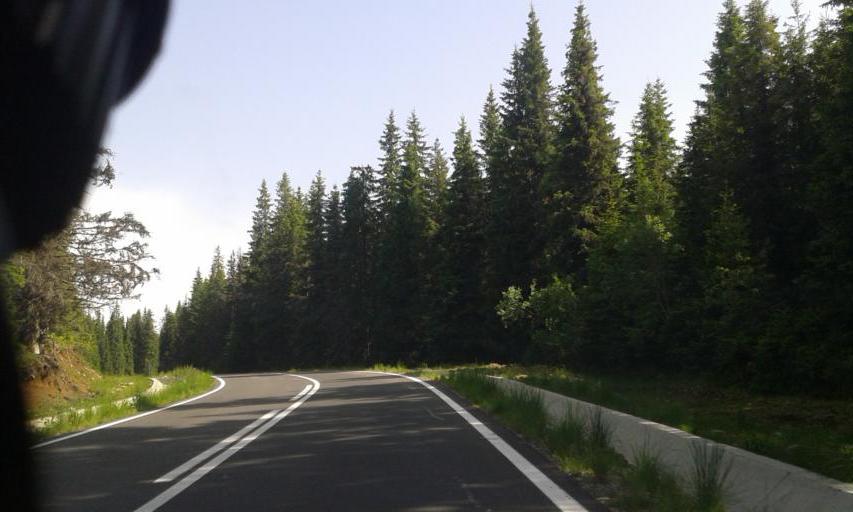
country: RO
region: Hunedoara
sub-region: Oras Petrila
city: Petrila
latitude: 45.4886
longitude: 23.6379
